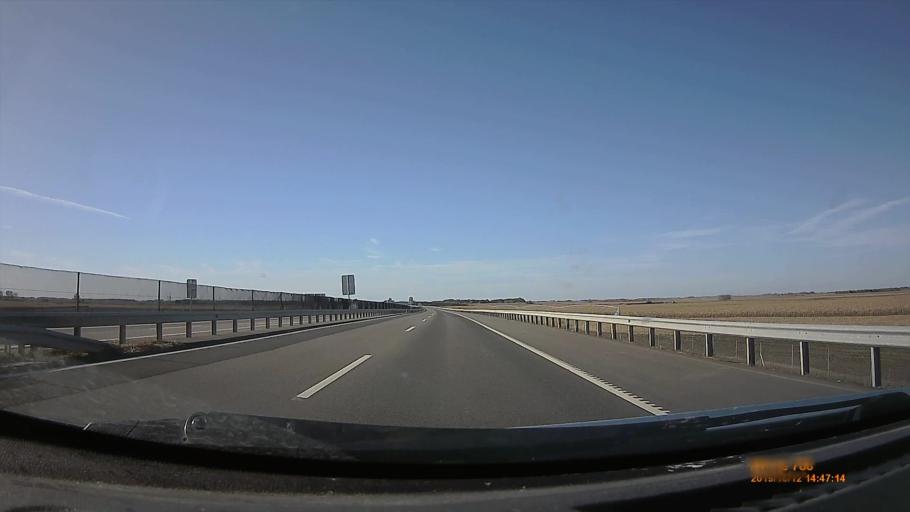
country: HU
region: Hajdu-Bihar
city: Berettyoujfalu
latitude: 47.2801
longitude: 21.5404
